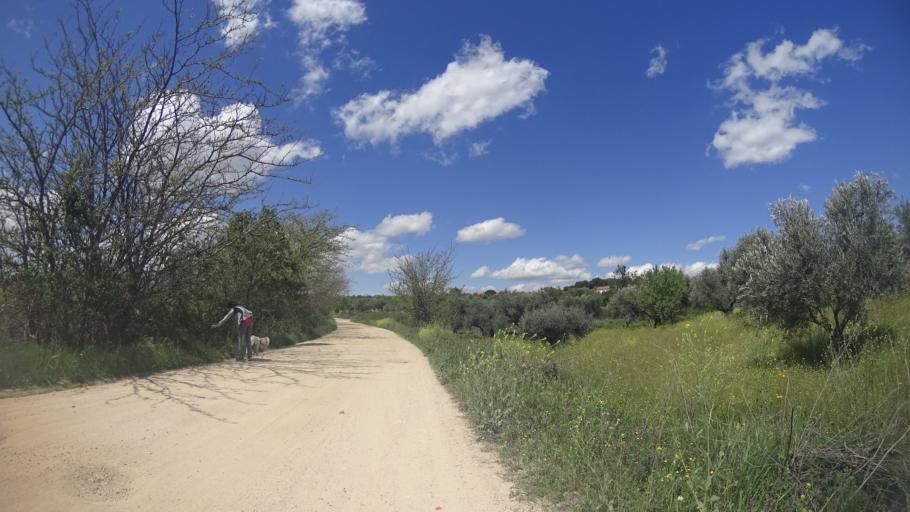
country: ES
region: Madrid
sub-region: Provincia de Madrid
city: San Martin de Valdeiglesias
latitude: 40.3659
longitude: -4.3871
